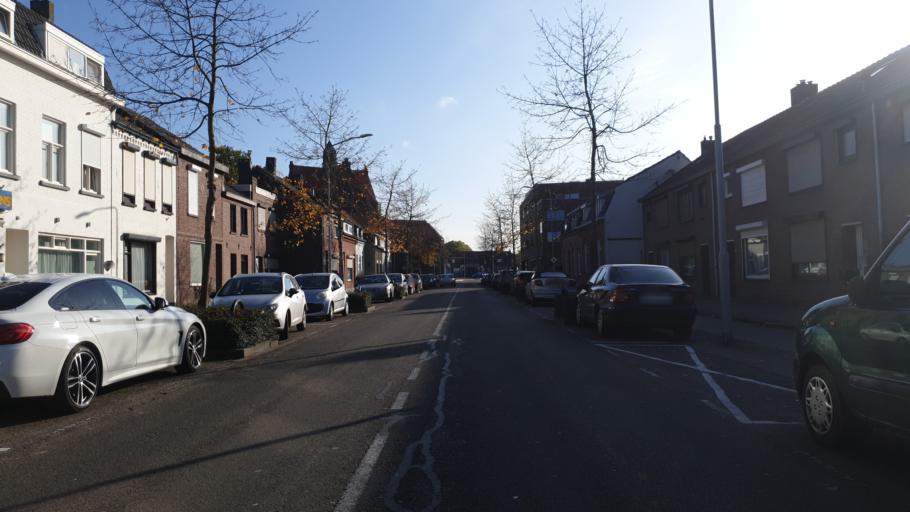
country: NL
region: Limburg
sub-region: Gemeente Venlo
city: Venlo
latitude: 51.3796
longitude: 6.1799
